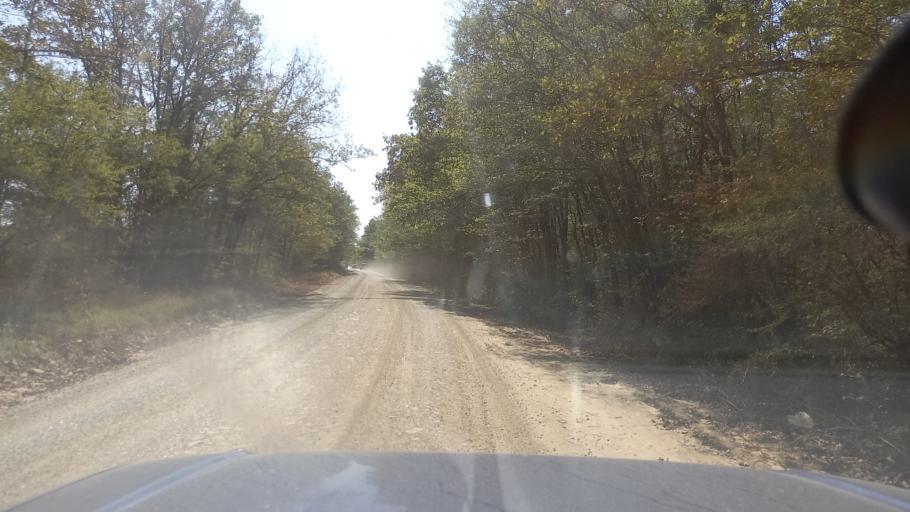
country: RU
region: Krasnodarskiy
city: Azovskaya
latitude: 44.6816
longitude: 38.6349
